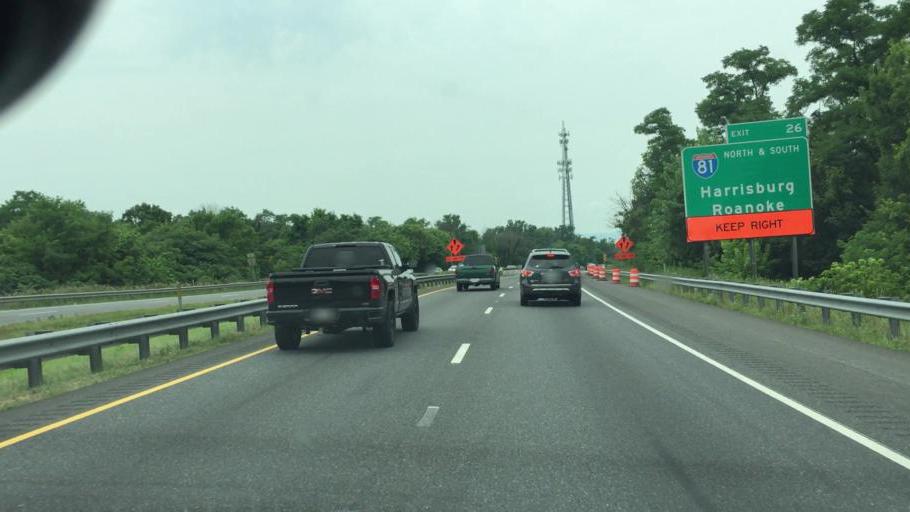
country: US
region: Maryland
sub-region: Washington County
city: Halfway
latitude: 39.6081
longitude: -77.7775
